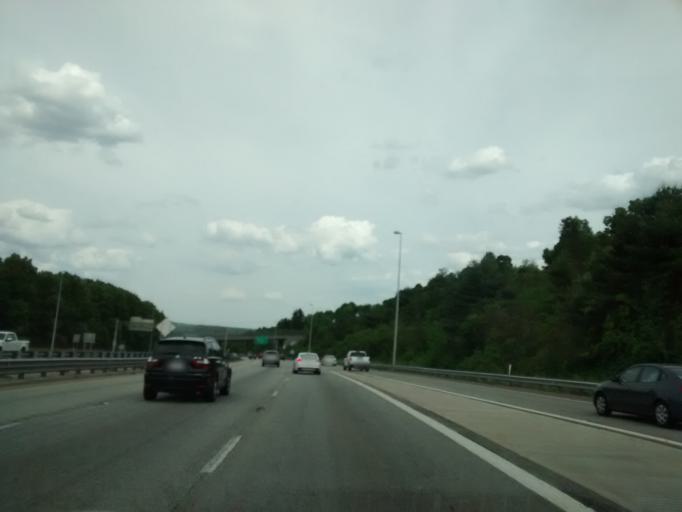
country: US
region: Massachusetts
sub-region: Worcester County
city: Worcester
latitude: 42.2902
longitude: -71.7824
